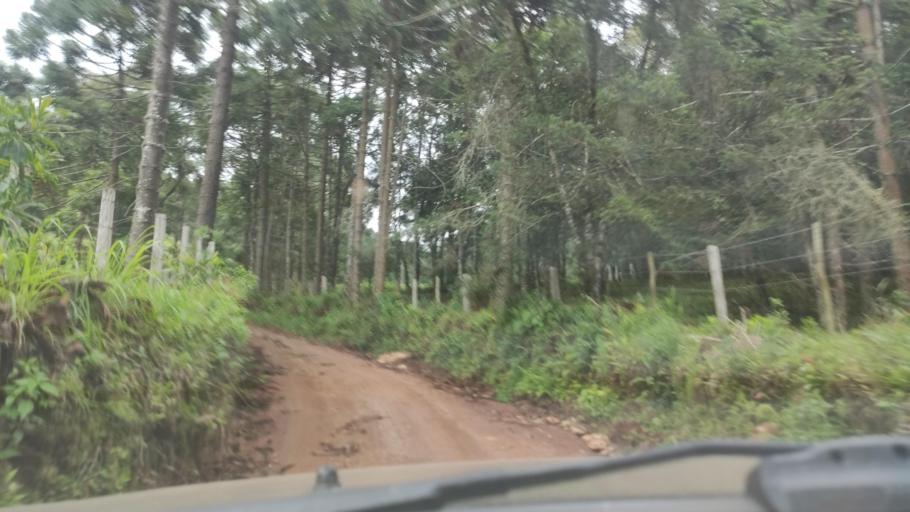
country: BR
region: Minas Gerais
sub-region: Paraisopolis
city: Paraisopolis
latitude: -22.7239
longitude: -45.8384
